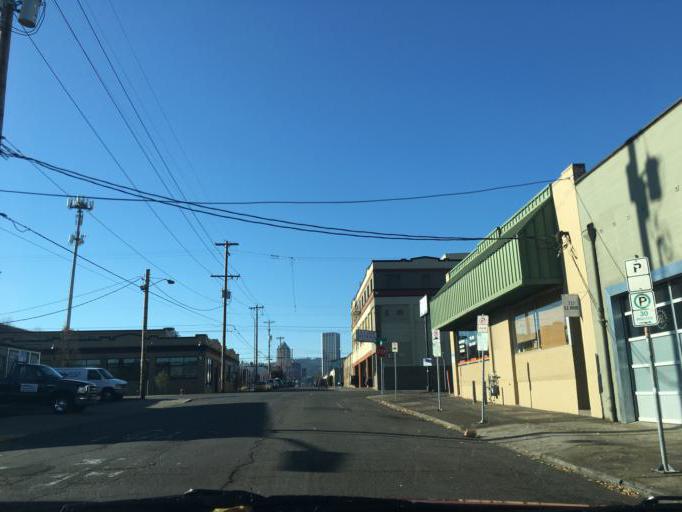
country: US
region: Oregon
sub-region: Multnomah County
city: Portland
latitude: 45.5136
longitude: -122.6581
